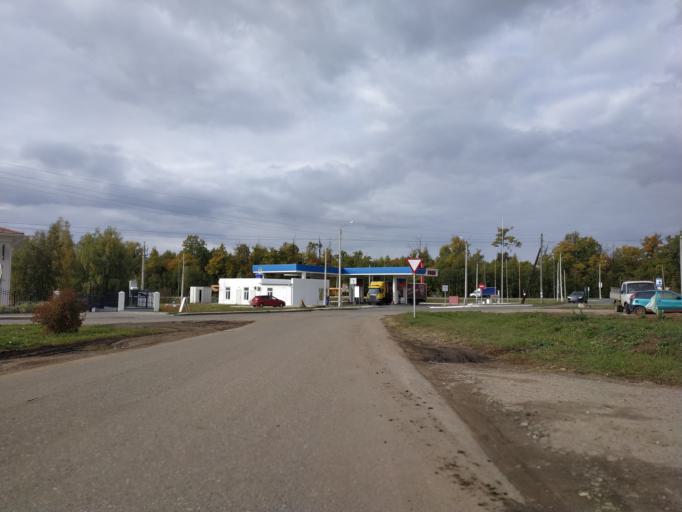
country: RU
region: Chuvashia
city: Ishley
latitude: 56.1325
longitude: 47.0865
